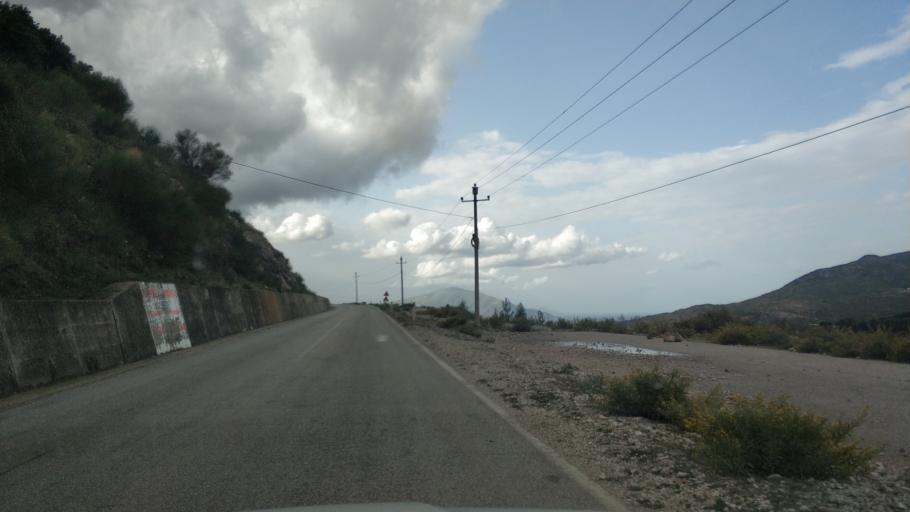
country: AL
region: Vlore
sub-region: Rrethi i Vlores
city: Orikum
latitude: 40.2625
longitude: 19.5221
